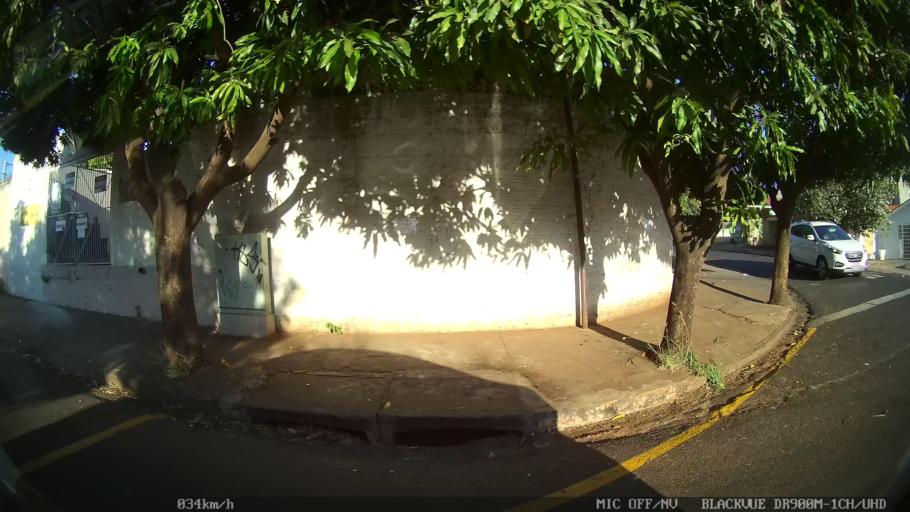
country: BR
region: Sao Paulo
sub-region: Sao Jose Do Rio Preto
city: Sao Jose do Rio Preto
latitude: -20.7913
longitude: -49.3488
